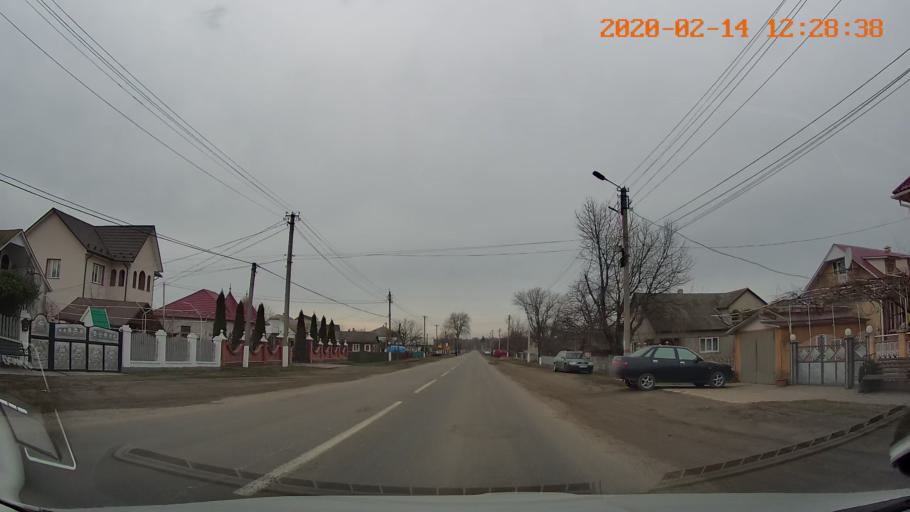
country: RO
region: Botosani
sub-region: Comuna Paltinis
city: Paltinis
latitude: 48.2580
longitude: 26.5945
